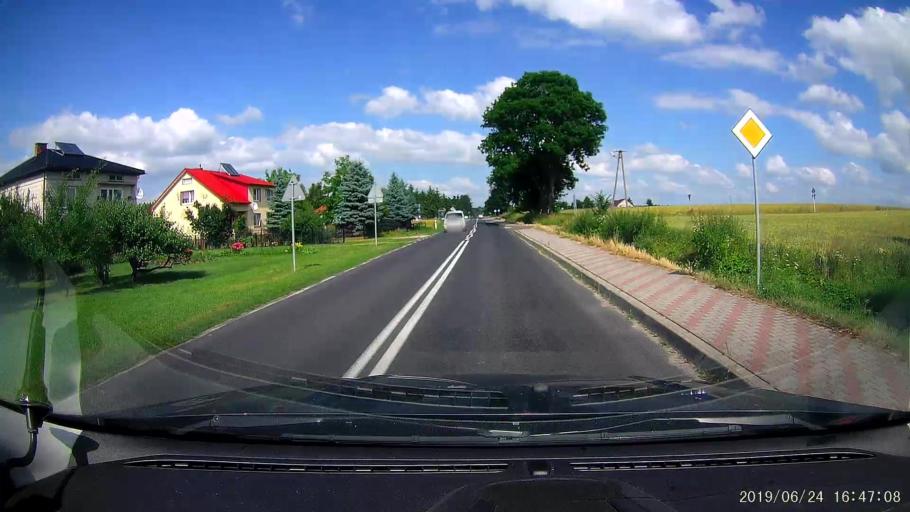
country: PL
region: Lublin Voivodeship
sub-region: Powiat tomaszowski
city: Laszczow
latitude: 50.5296
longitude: 23.6946
